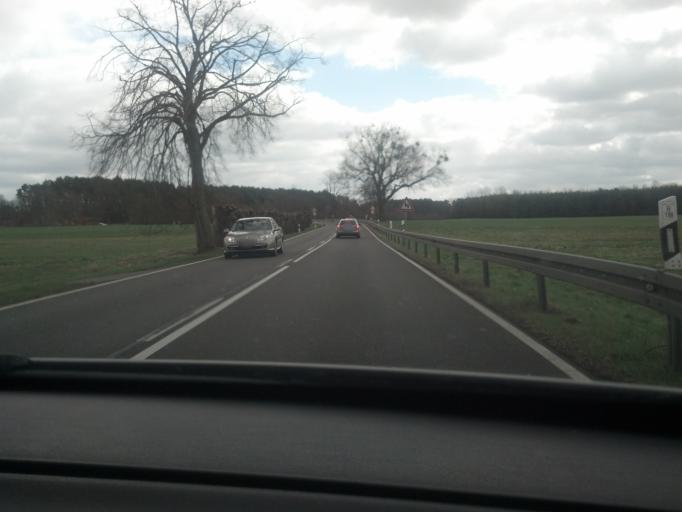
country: DE
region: Mecklenburg-Vorpommern
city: Rechlin
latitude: 53.2917
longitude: 12.7889
